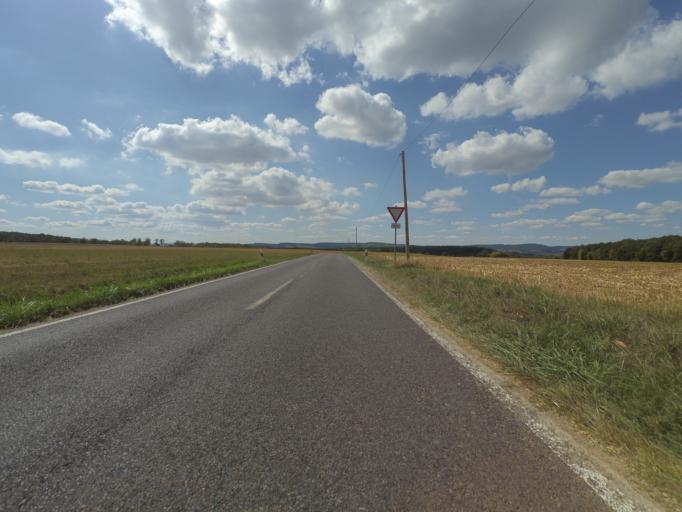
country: DE
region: Rheinland-Pfalz
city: Palzem
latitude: 49.5656
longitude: 6.3922
